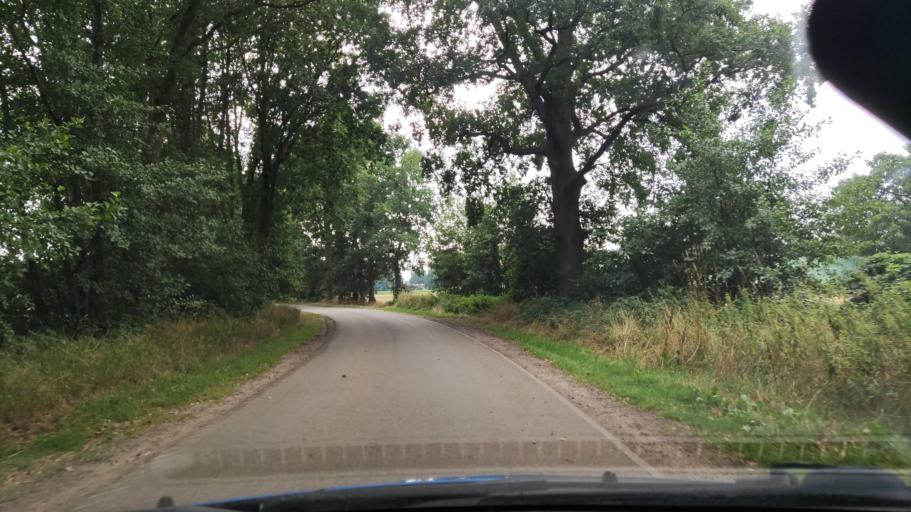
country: DE
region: Lower Saxony
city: Wittorf
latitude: 53.3386
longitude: 10.3734
